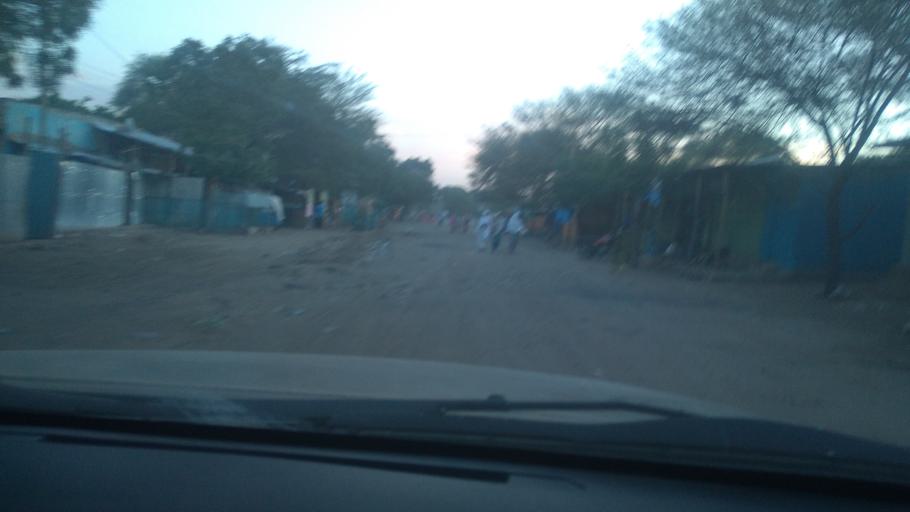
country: ET
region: Oromiya
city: Asbe Teferi
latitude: 9.2348
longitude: 40.7566
